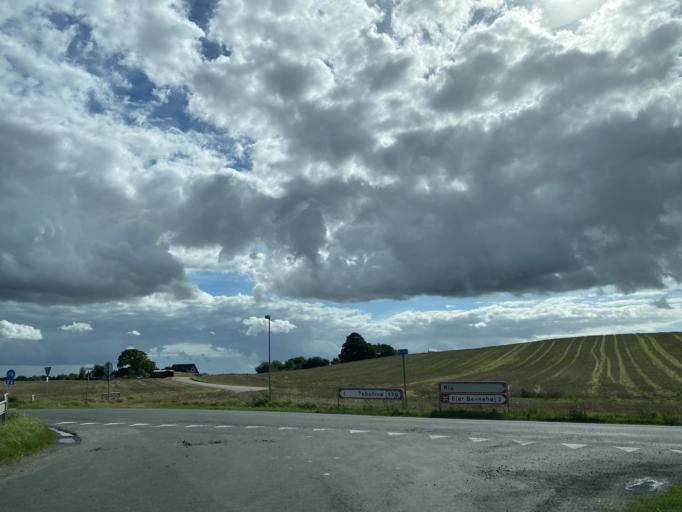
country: DK
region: Central Jutland
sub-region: Skanderborg Kommune
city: Skanderborg
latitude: 55.9768
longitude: 9.8553
